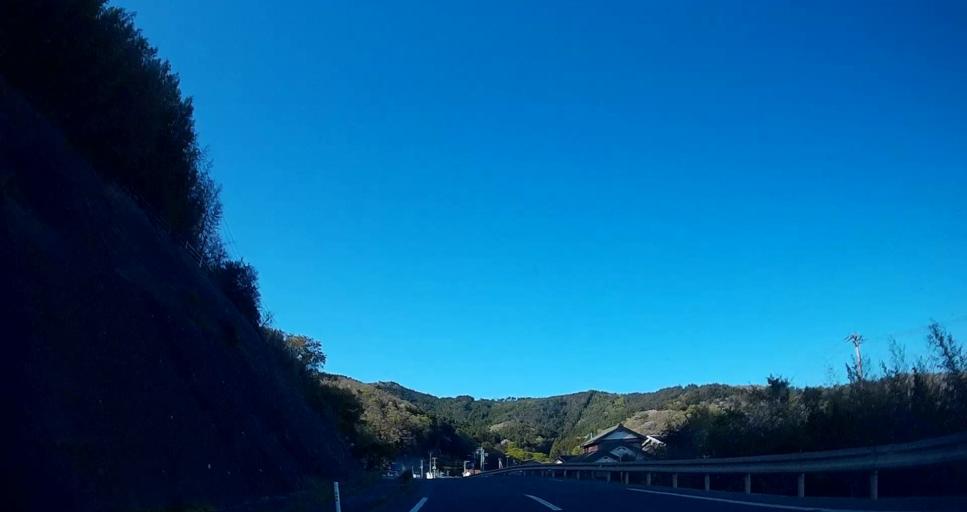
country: JP
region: Miyagi
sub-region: Oshika Gun
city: Onagawa Cho
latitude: 38.4353
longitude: 141.3857
